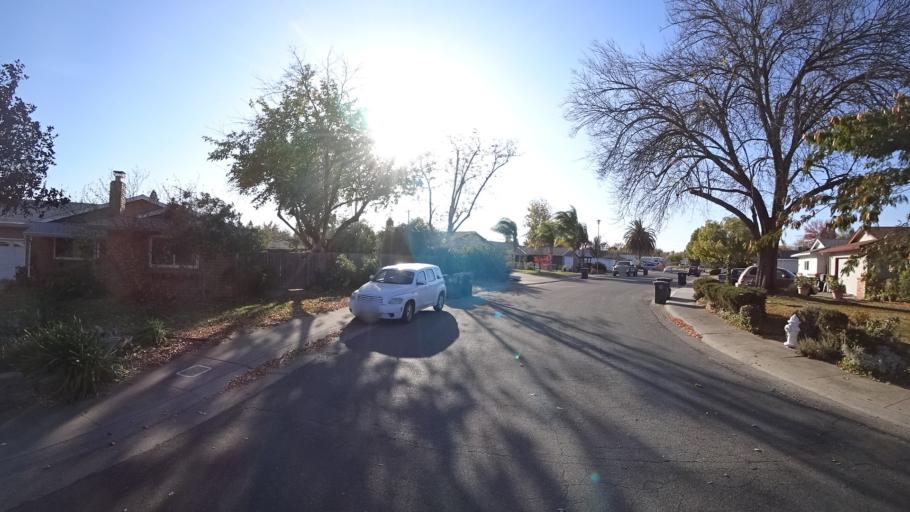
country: US
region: California
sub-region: Sacramento County
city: Antelope
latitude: 38.7034
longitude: -121.3060
